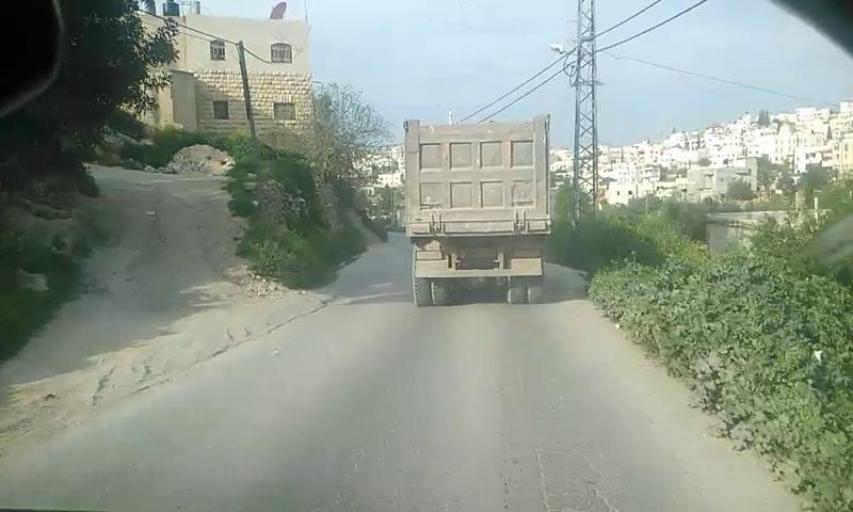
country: PS
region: West Bank
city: Bayt Ula
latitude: 31.5908
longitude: 35.0262
